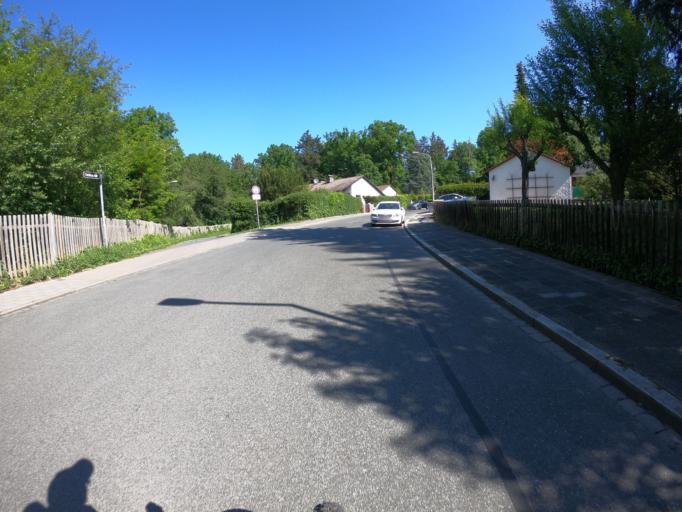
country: DE
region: Bavaria
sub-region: Regierungsbezirk Mittelfranken
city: Stein
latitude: 49.4115
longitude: 11.0221
